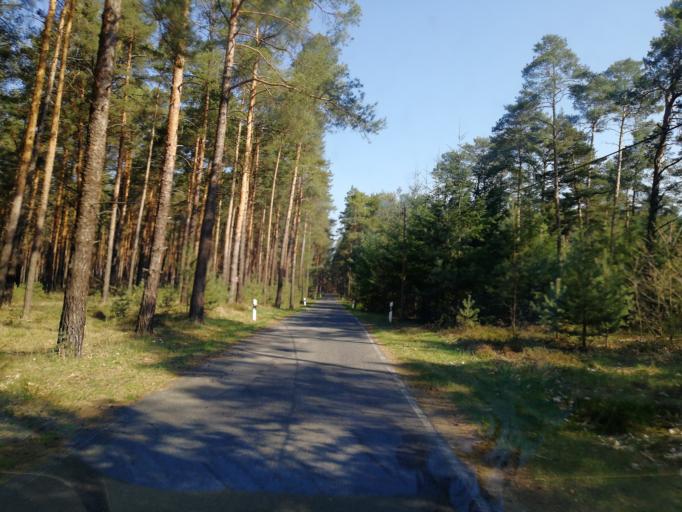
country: DE
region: Brandenburg
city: Bronkow
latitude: 51.6792
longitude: 13.8643
